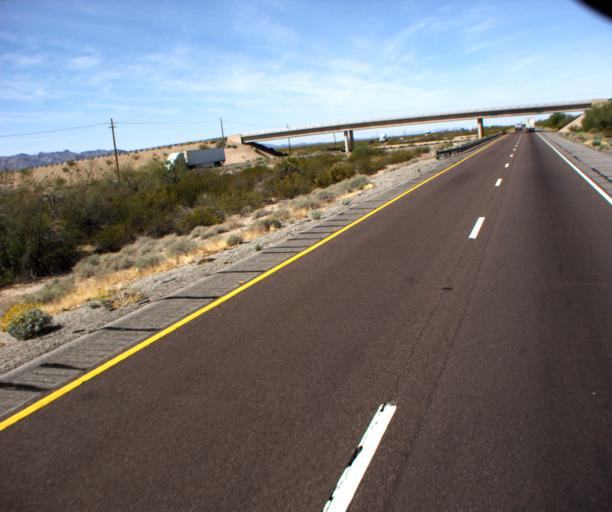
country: US
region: Arizona
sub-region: La Paz County
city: Salome
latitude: 33.5610
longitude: -113.2985
